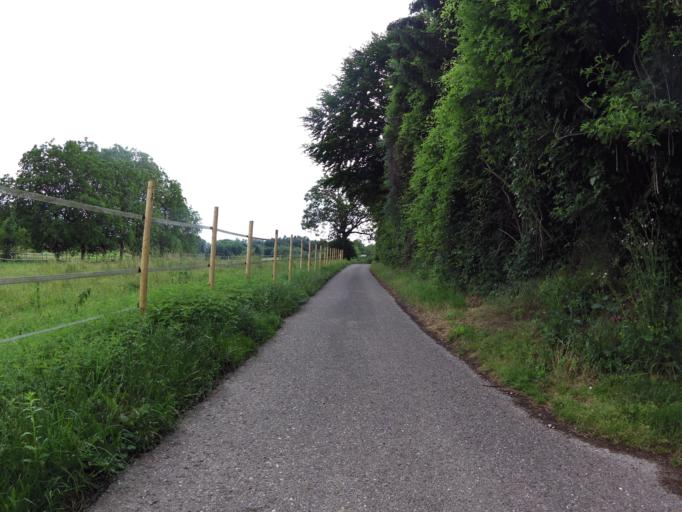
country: DE
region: Baden-Wuerttemberg
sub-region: Freiburg Region
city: Lahr
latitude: 48.3594
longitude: 7.8582
